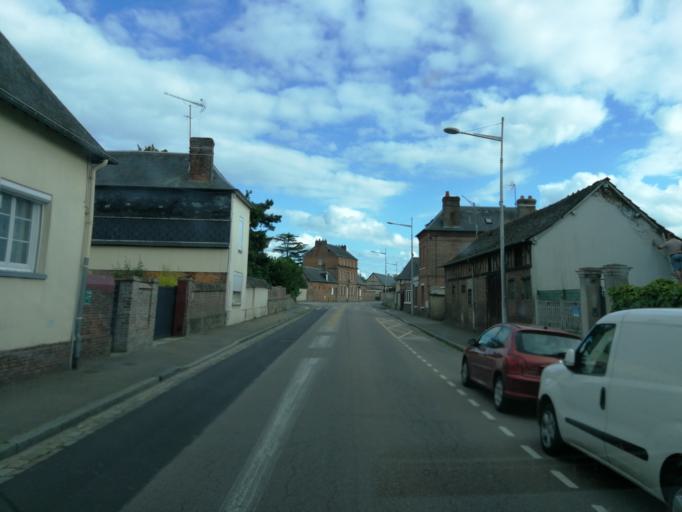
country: FR
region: Haute-Normandie
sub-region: Departement de l'Eure
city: Le Neubourg
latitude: 49.1456
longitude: 0.9021
